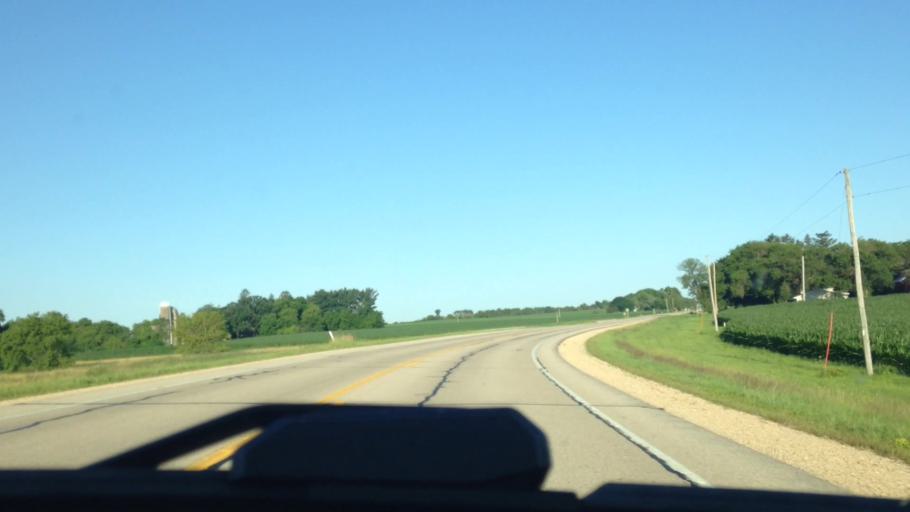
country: US
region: Wisconsin
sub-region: Columbia County
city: Rio
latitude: 43.3329
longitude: -89.2621
